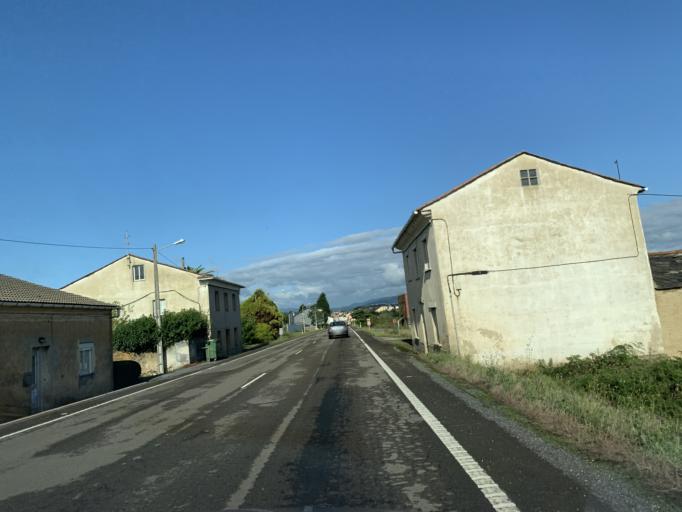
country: ES
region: Galicia
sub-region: Provincia de Lugo
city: Barreiros
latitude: 43.5431
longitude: -7.1817
